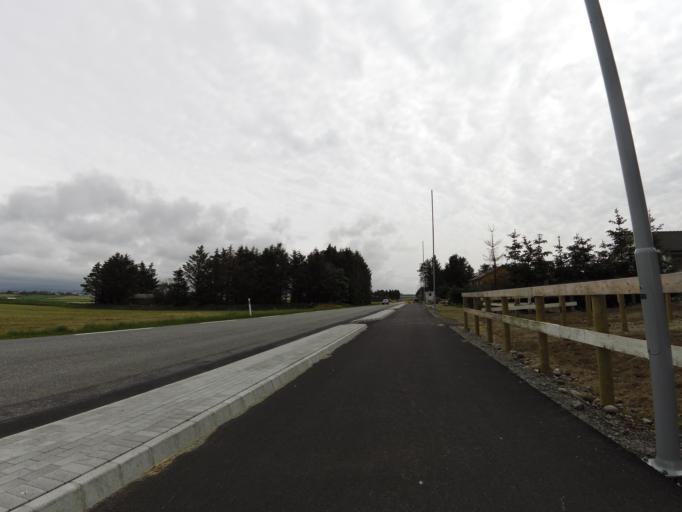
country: NO
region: Rogaland
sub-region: Ha
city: Naerbo
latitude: 58.6905
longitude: 5.5583
